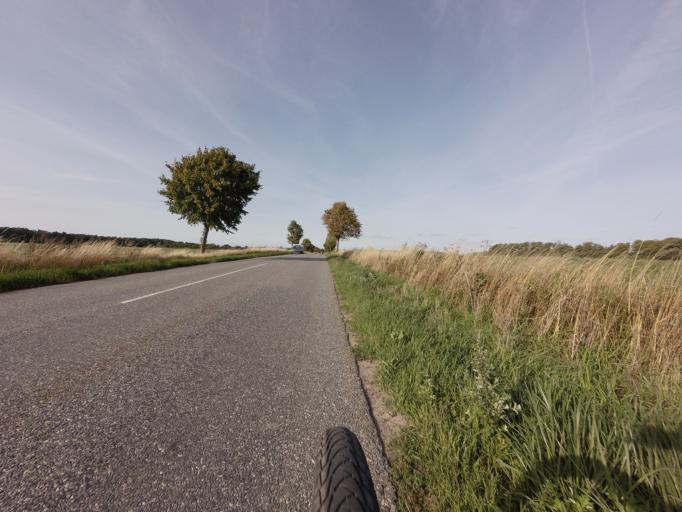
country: DK
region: Zealand
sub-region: Faxe Kommune
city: Fakse Ladeplads
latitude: 55.2421
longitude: 12.2175
